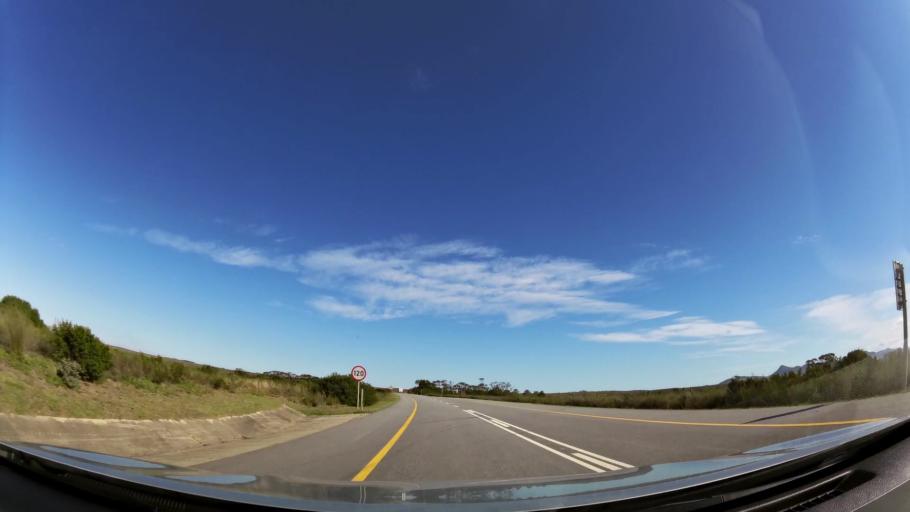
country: ZA
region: Eastern Cape
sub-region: Cacadu District Municipality
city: Kruisfontein
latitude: -34.0326
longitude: 24.5945
